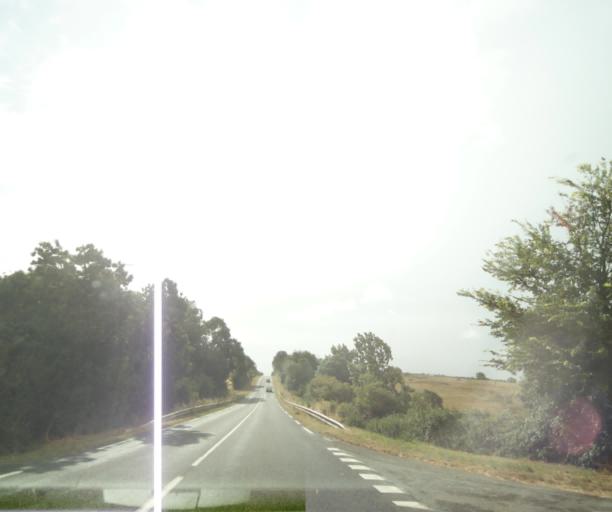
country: FR
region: Pays de la Loire
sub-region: Departement de la Vendee
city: Moutiers-les-Mauxfaits
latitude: 46.4563
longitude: -1.4295
